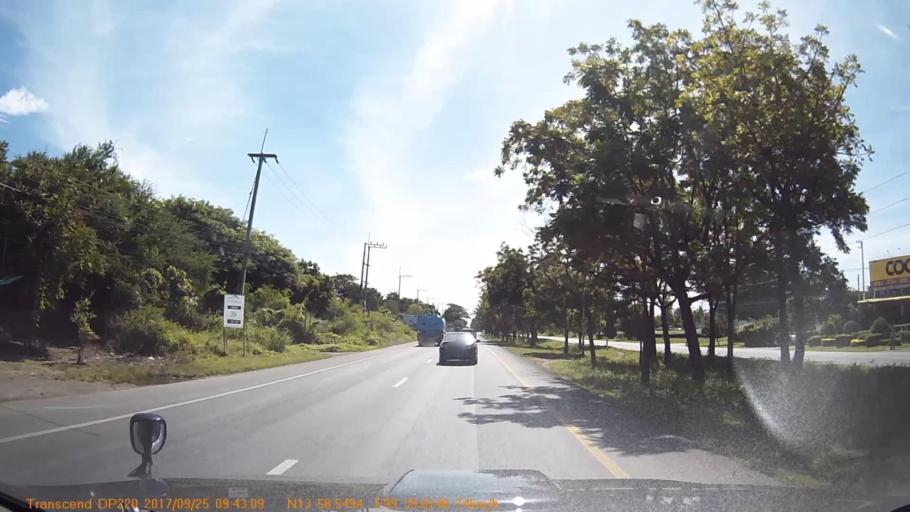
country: TH
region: Kanchanaburi
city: Tha Muang
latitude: 13.9758
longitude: 99.6638
